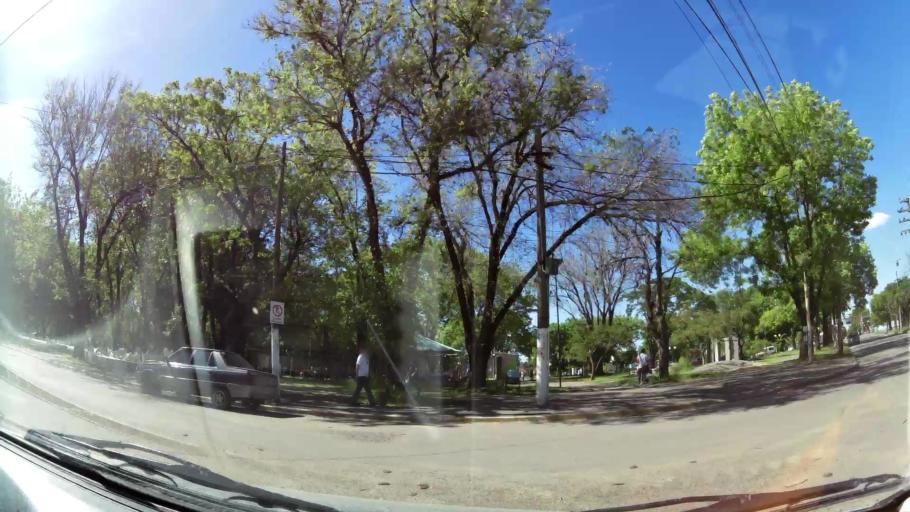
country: AR
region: Buenos Aires
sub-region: Partido de Almirante Brown
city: Adrogue
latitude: -34.7979
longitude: -58.3582
